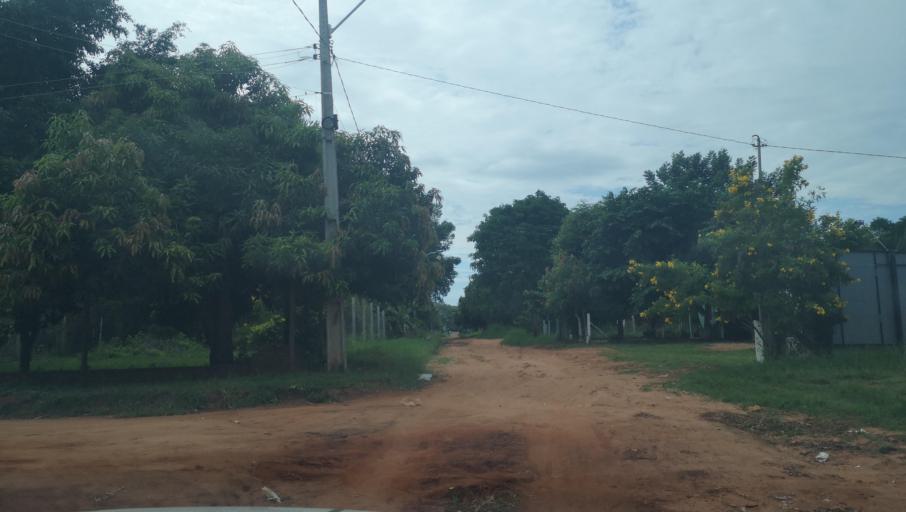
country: PY
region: San Pedro
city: Capiibary
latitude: -24.7253
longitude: -56.0227
